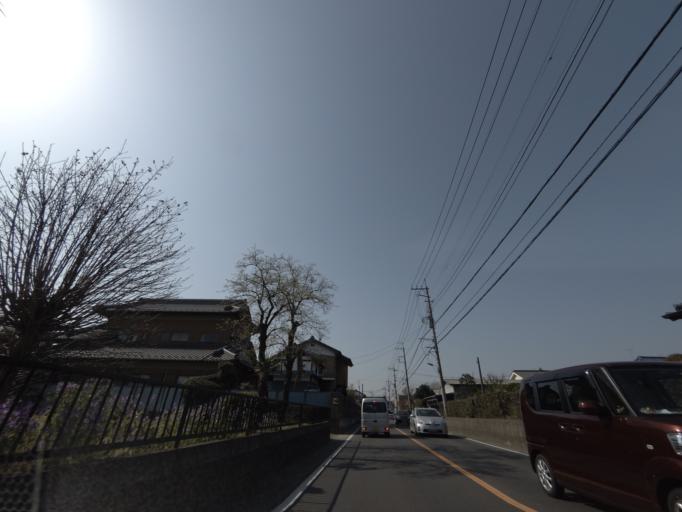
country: JP
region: Saitama
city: Yono
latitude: 35.8788
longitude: 139.5981
